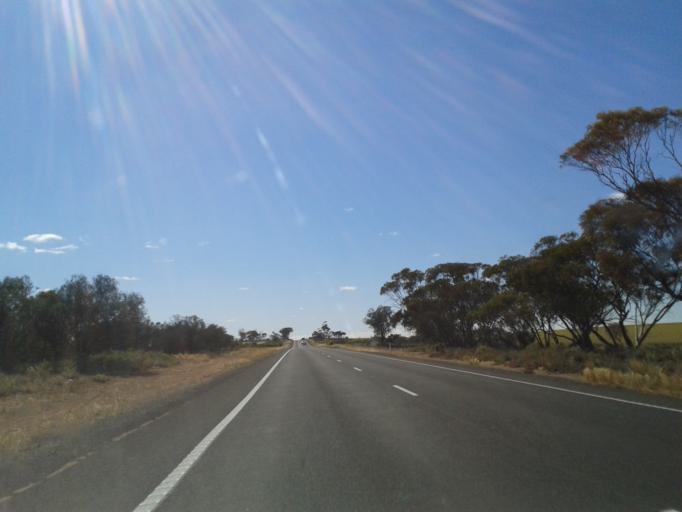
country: AU
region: South Australia
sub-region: Renmark Paringa
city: Renmark
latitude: -34.2747
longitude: 141.2467
